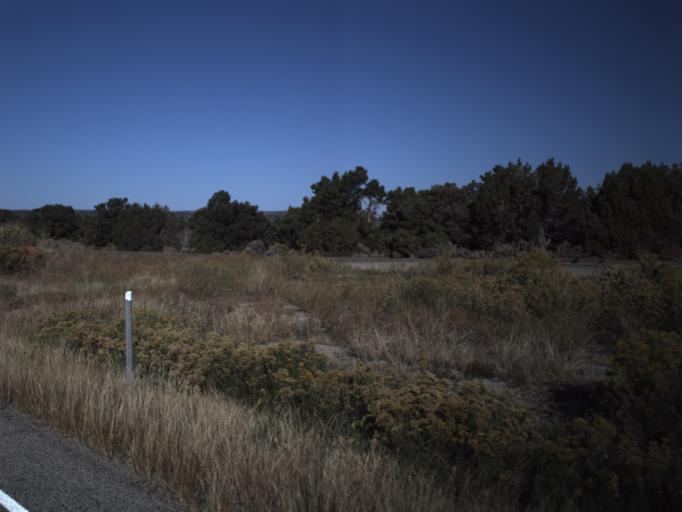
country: US
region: Utah
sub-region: San Juan County
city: Blanding
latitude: 37.5406
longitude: -109.9633
